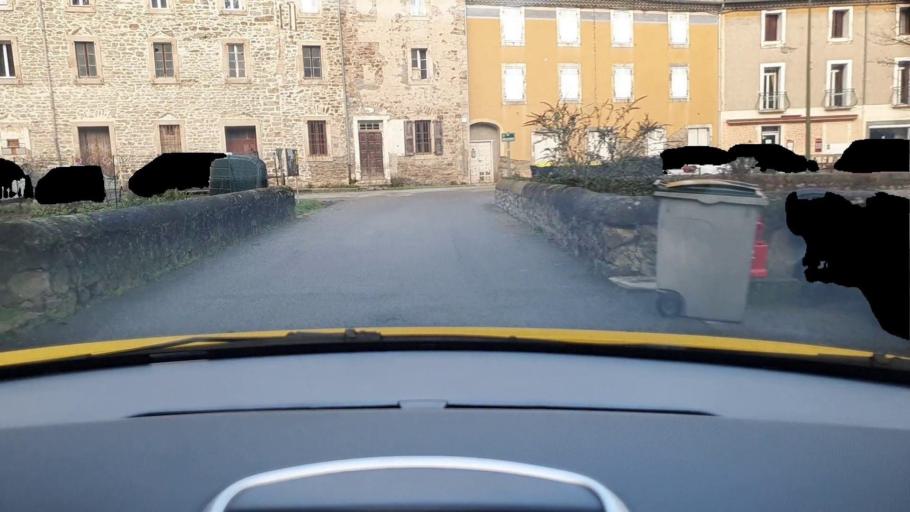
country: FR
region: Languedoc-Roussillon
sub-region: Departement du Gard
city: Branoux-les-Taillades
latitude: 44.2881
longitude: 4.0084
